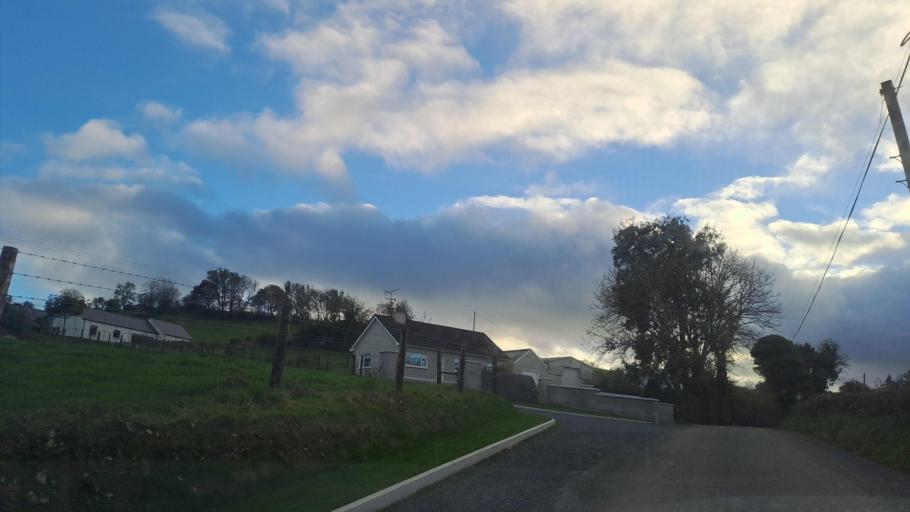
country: IE
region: Ulster
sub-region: County Monaghan
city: Castleblayney
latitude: 54.0422
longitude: -6.7998
